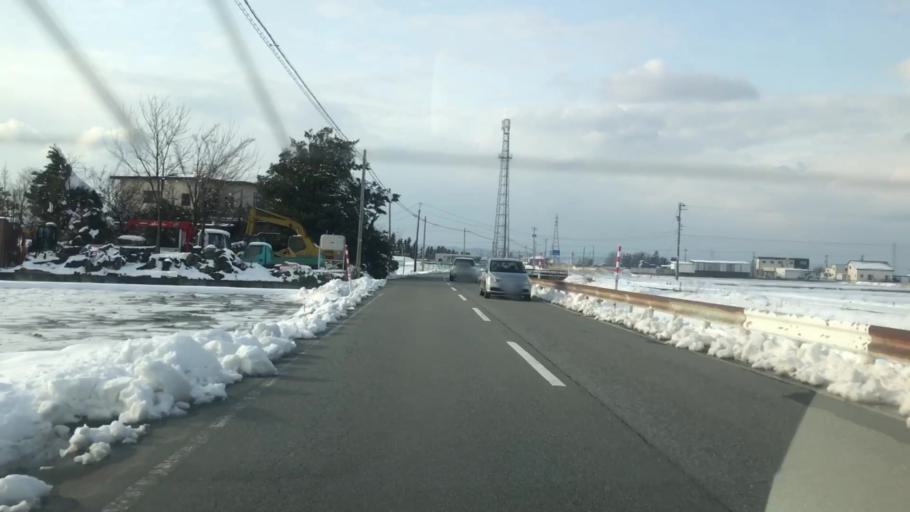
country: JP
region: Toyama
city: Toyama-shi
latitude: 36.6390
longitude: 137.2610
